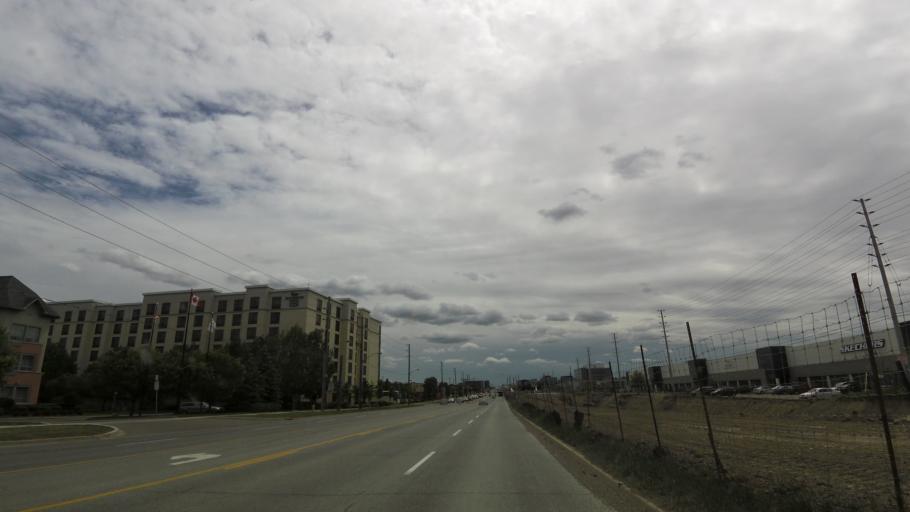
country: CA
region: Ontario
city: Etobicoke
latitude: 43.6535
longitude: -79.6012
